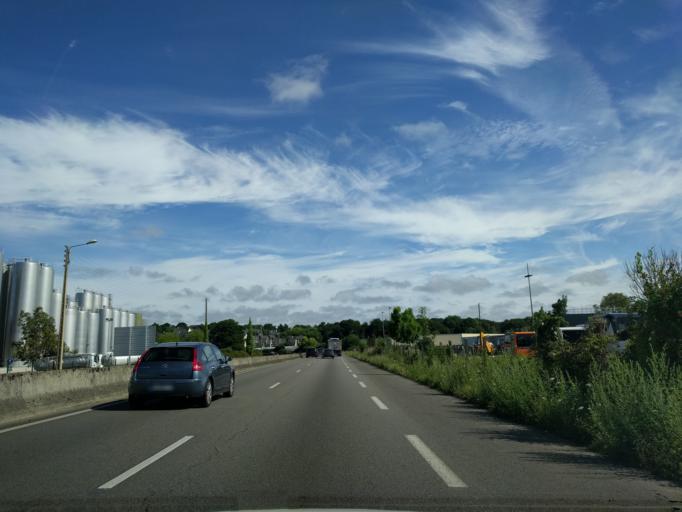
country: FR
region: Brittany
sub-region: Departement du Finistere
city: Quimper
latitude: 47.9961
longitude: -4.0729
